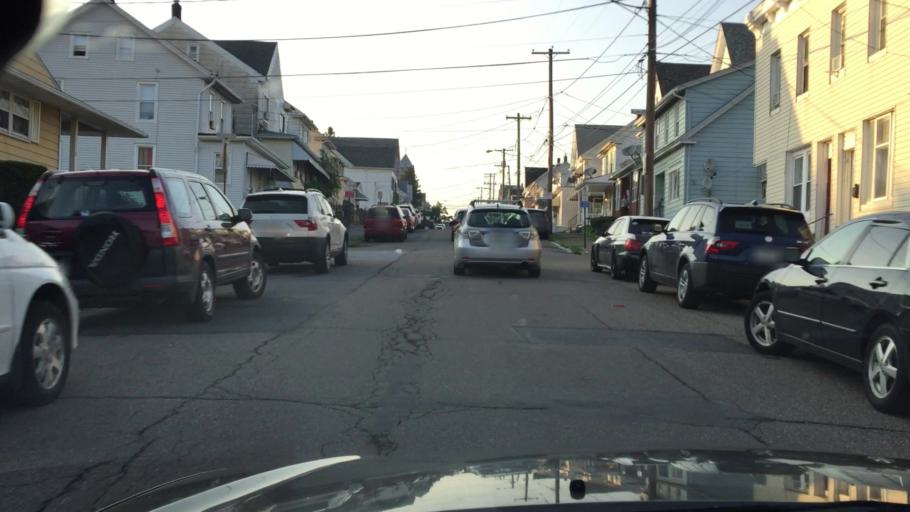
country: US
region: Pennsylvania
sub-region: Luzerne County
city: Hazleton
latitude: 40.9628
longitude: -75.9699
